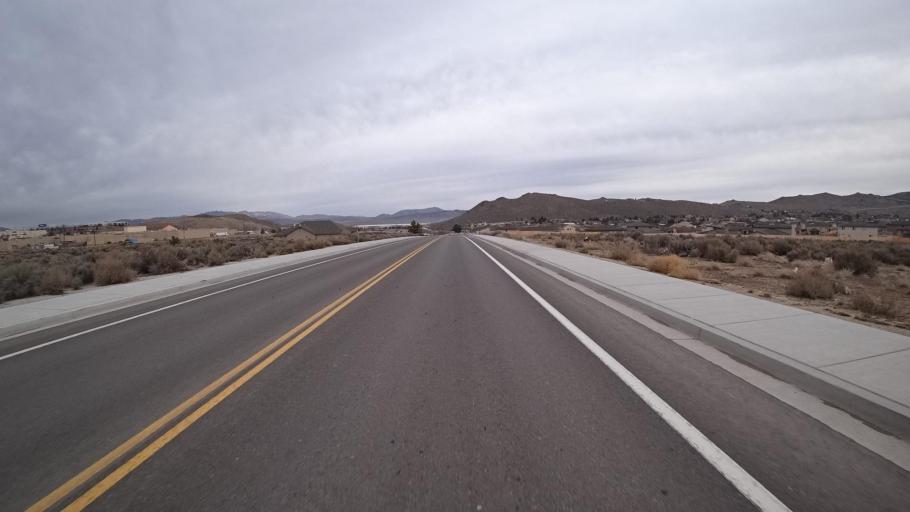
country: US
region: Nevada
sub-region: Washoe County
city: Golden Valley
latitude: 39.6103
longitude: -119.8449
